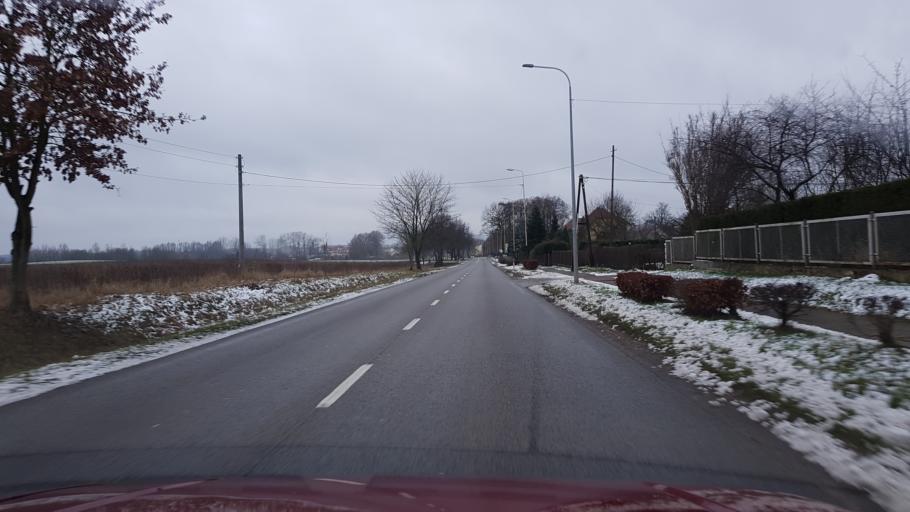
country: PL
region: West Pomeranian Voivodeship
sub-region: Powiat goleniowski
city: Nowogard
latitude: 53.6629
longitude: 15.1580
